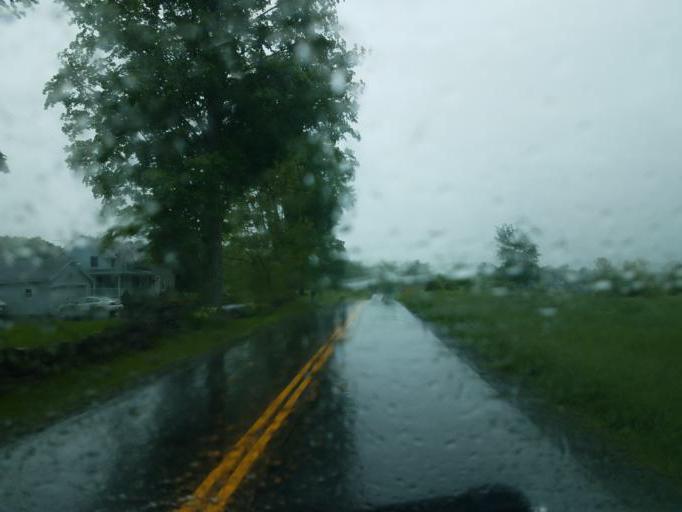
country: US
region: New York
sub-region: Herkimer County
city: Frankfort
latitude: 42.9155
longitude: -75.1435
